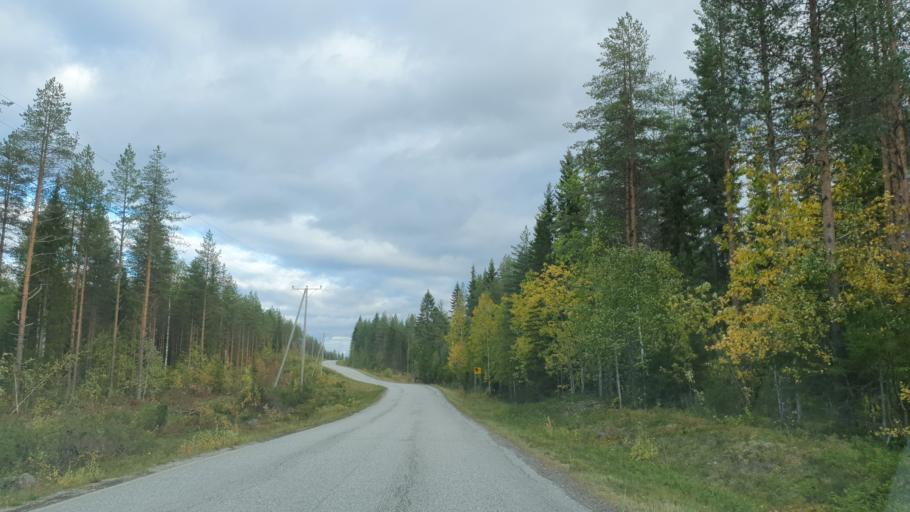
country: FI
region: Kainuu
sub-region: Kehys-Kainuu
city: Kuhmo
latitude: 63.9518
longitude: 29.8371
